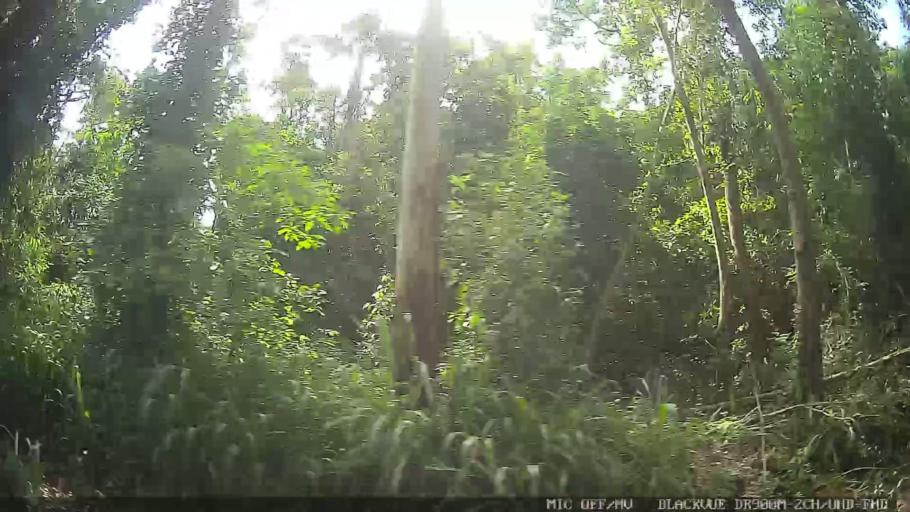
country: BR
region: Sao Paulo
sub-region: Mogi das Cruzes
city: Mogi das Cruzes
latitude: -23.4756
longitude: -46.2545
